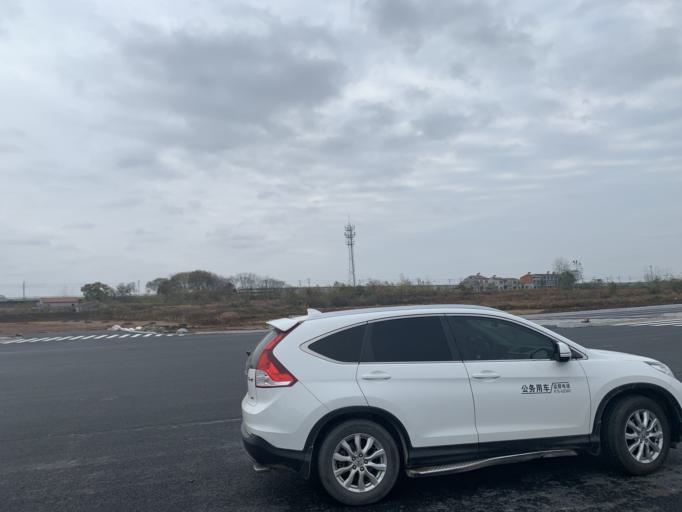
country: CN
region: Hubei
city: Anlu
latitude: 31.2498
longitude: 113.6522
